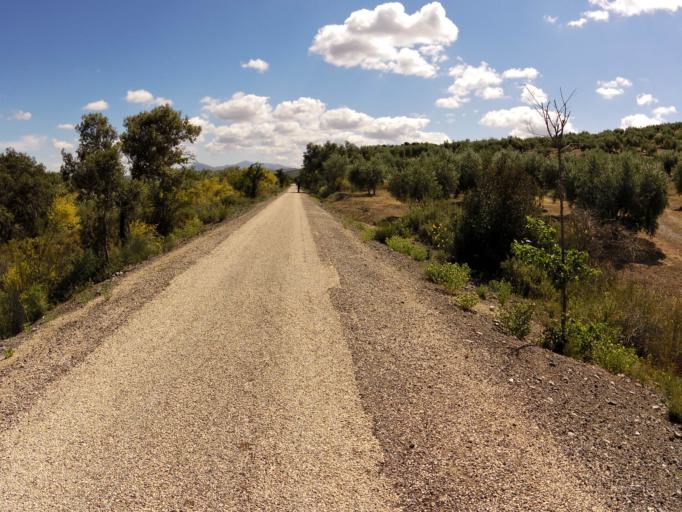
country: ES
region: Andalusia
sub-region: Provincia de Jaen
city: Alcaudete
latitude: 37.6193
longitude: -4.1062
